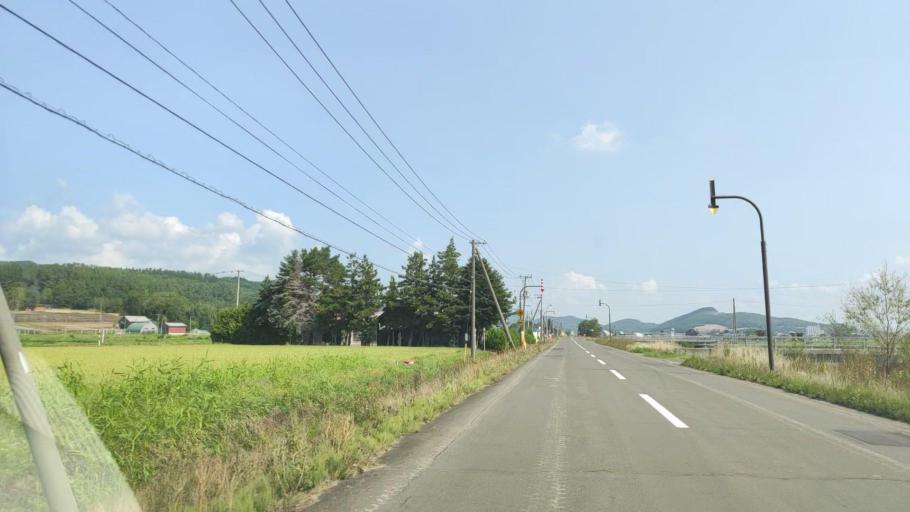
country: JP
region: Hokkaido
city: Shimo-furano
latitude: 43.3751
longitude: 142.3892
